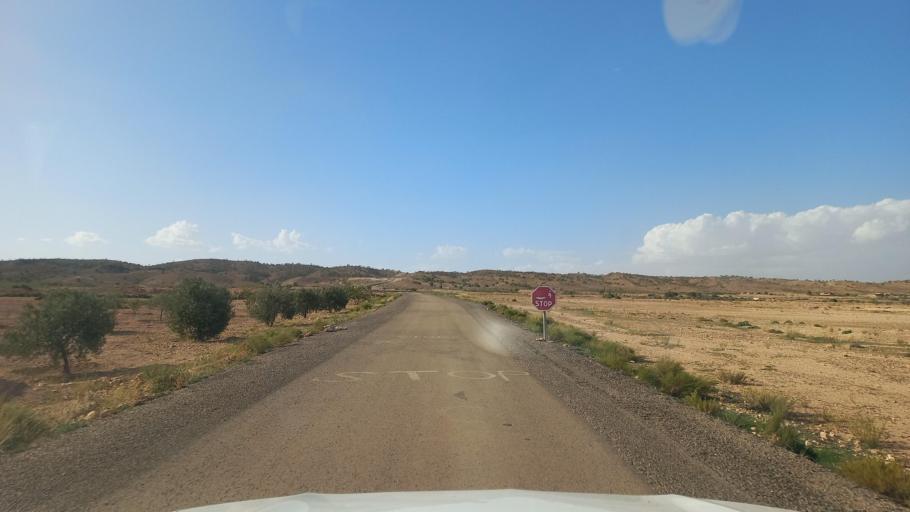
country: TN
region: Al Qasrayn
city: Sbiba
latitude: 35.3494
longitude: 8.9882
